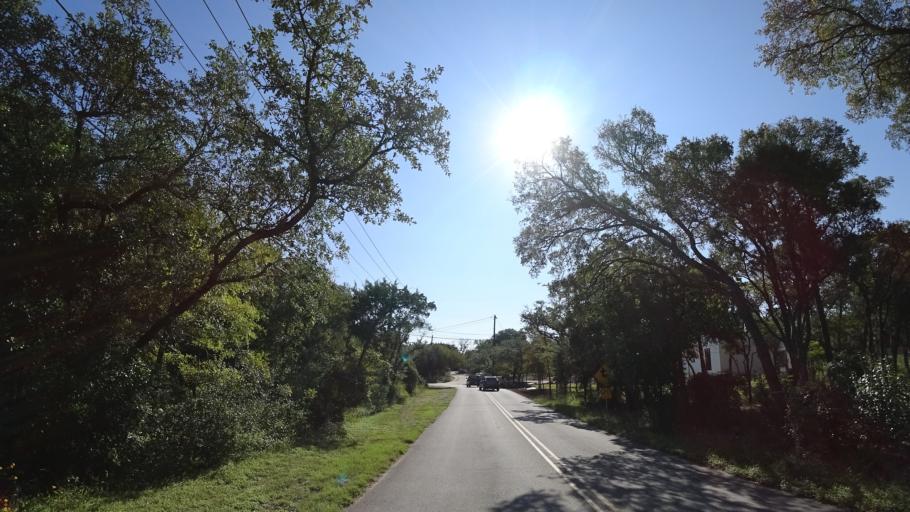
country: US
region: Texas
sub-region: Travis County
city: Rollingwood
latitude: 30.2655
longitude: -97.8117
